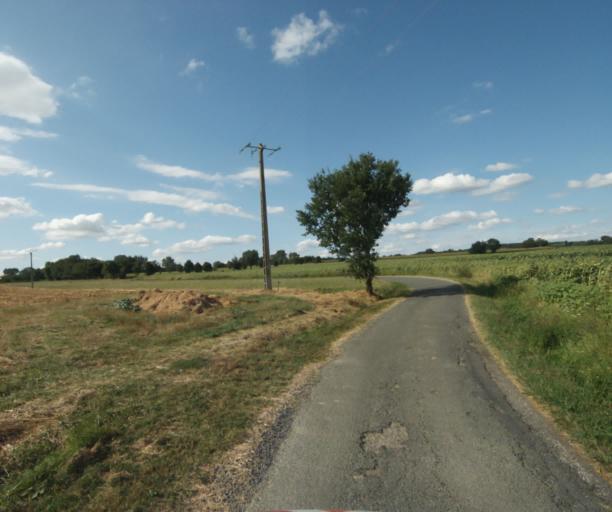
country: FR
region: Midi-Pyrenees
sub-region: Departement du Tarn
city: Puylaurens
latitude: 43.5357
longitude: 1.9879
